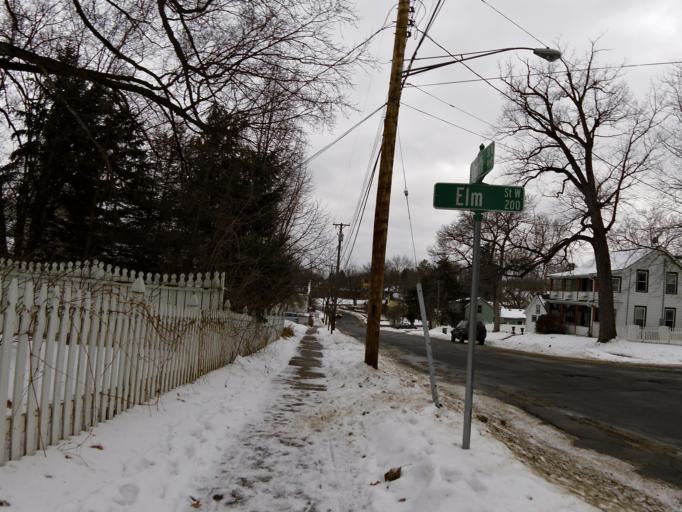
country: US
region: Minnesota
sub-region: Washington County
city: Stillwater
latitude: 45.0632
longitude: -92.8127
